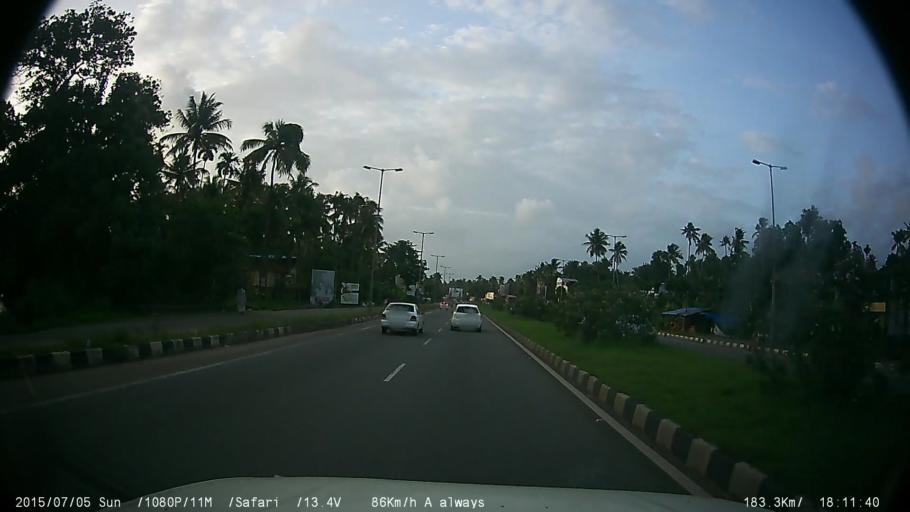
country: IN
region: Kerala
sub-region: Thrissur District
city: Kizhake Chalakudi
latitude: 10.3580
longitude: 76.3164
